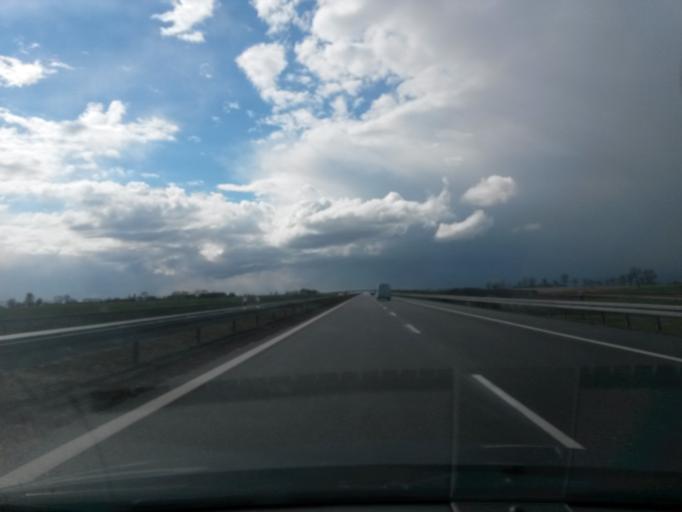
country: PL
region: Greater Poland Voivodeship
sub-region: Powiat wrzesinski
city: Wrzesnia
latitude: 52.3184
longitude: 17.4855
